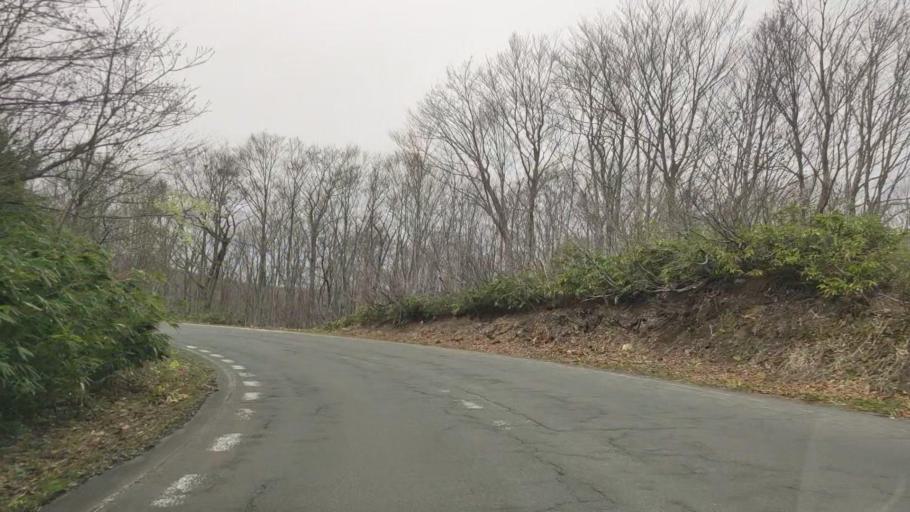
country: JP
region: Aomori
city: Aomori Shi
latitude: 40.6578
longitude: 140.9557
